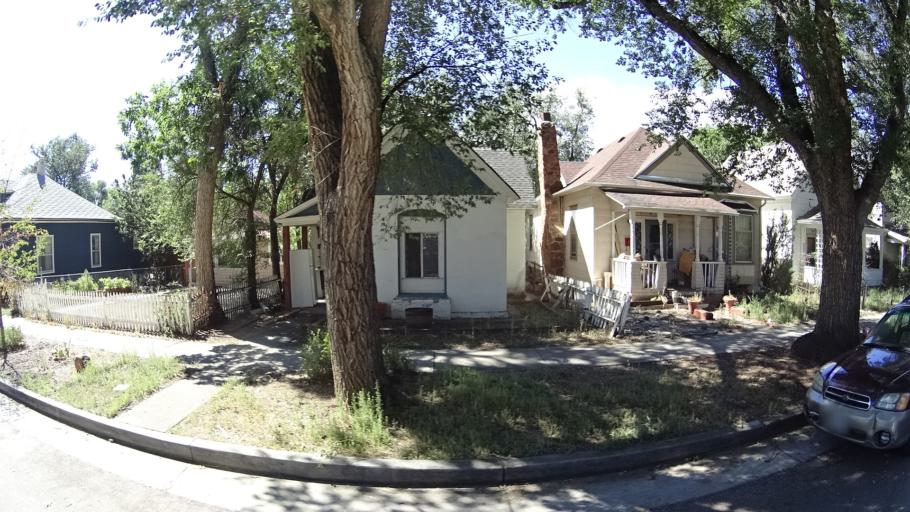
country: US
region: Colorado
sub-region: El Paso County
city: Colorado Springs
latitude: 38.8479
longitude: -104.8584
